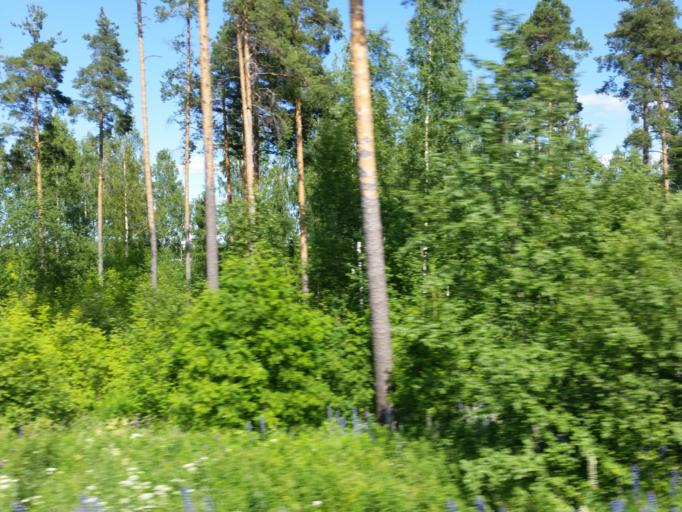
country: FI
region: Northern Savo
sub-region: Varkaus
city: Varkaus
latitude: 62.3064
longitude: 27.8595
